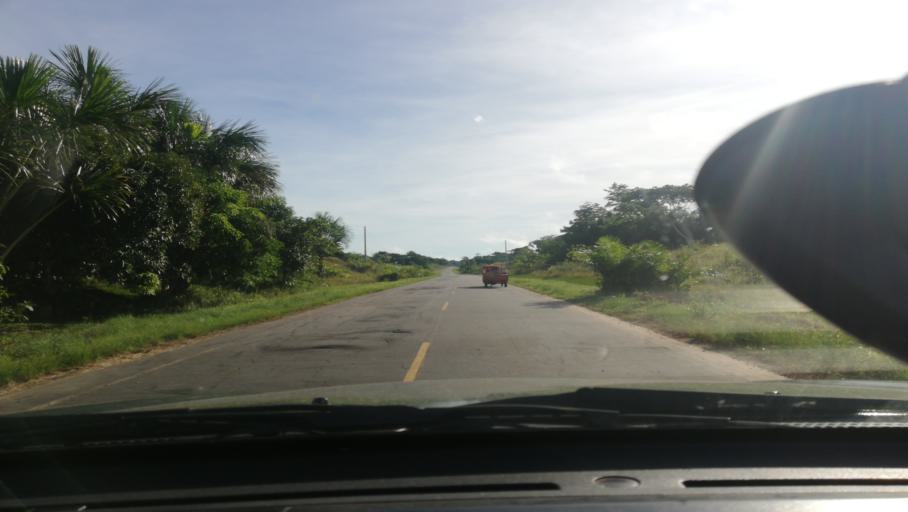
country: PE
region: Loreto
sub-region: Provincia de Loreto
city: Nauta
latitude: -4.3406
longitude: -73.5384
